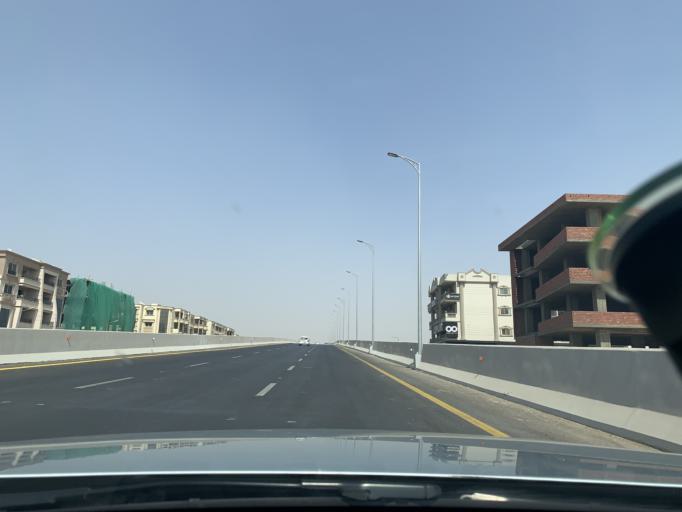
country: EG
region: Muhafazat al Qalyubiyah
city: Al Khankah
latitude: 30.0911
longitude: 31.3743
